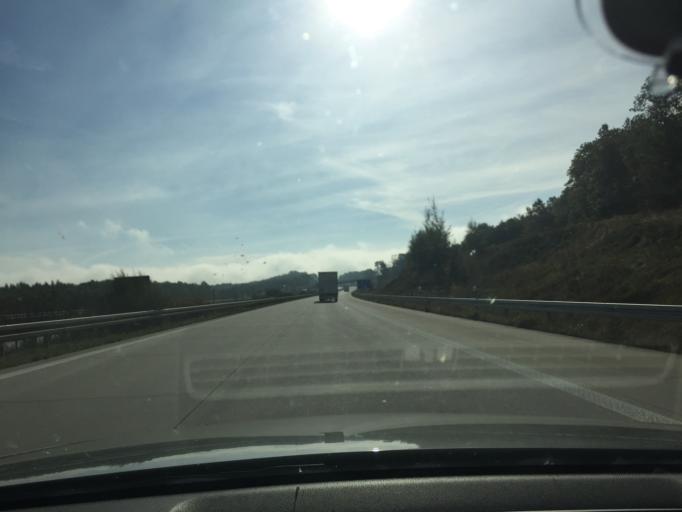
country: DE
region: Saxony
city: Liebstadt
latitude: 50.8467
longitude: 13.8812
